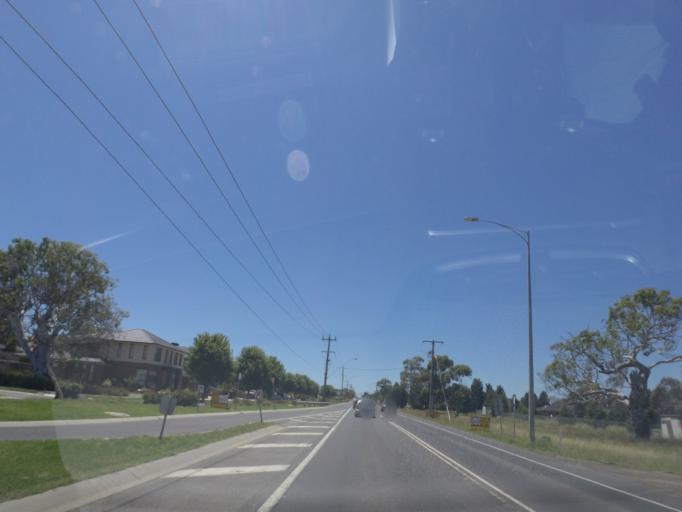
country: AU
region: Victoria
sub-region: Whittlesea
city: Epping
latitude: -37.6335
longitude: 145.0270
